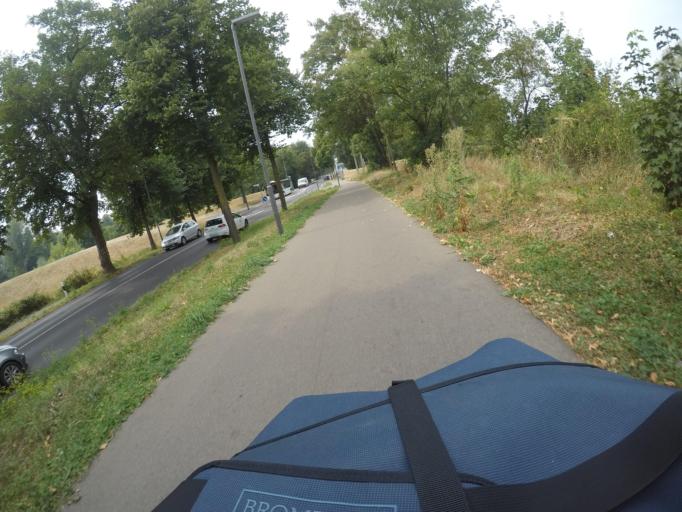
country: DE
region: North Rhine-Westphalia
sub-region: Regierungsbezirk Dusseldorf
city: Neuss
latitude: 51.1804
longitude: 6.7334
